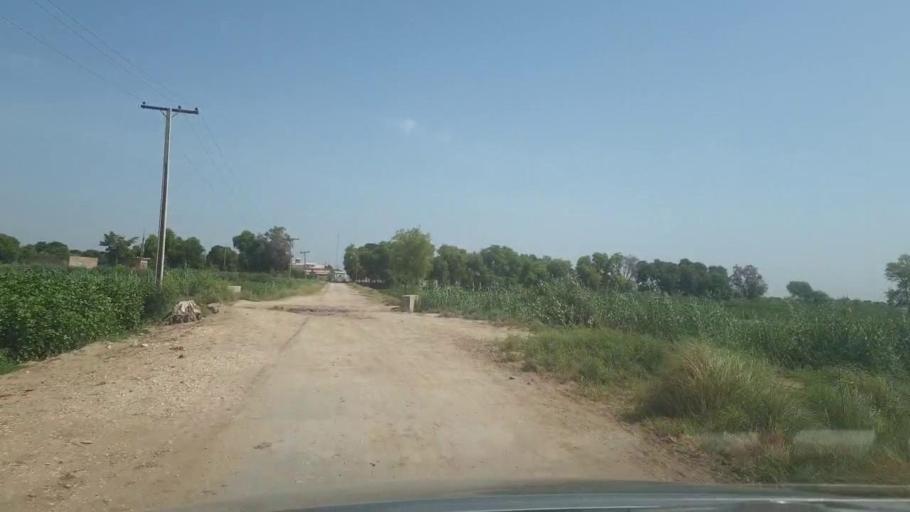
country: PK
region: Sindh
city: Rohri
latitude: 27.4038
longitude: 69.0813
